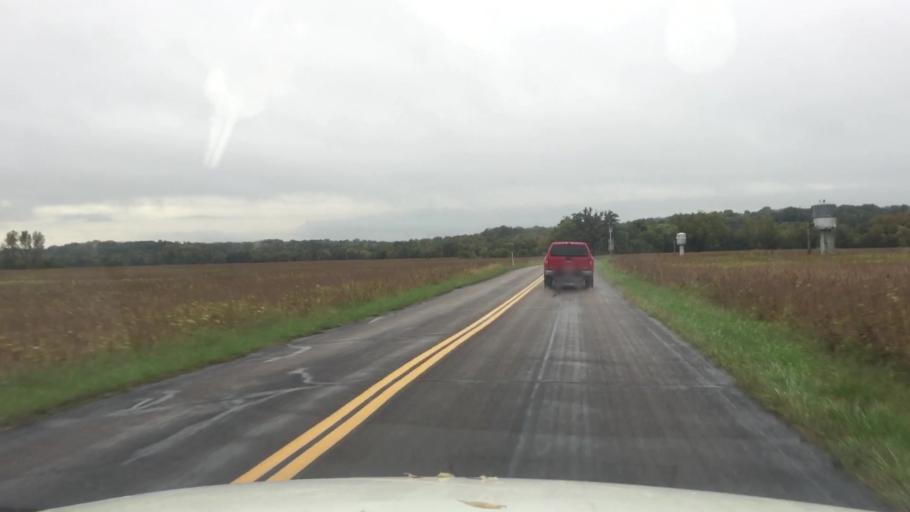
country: US
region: Missouri
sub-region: Boone County
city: Columbia
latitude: 38.8949
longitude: -92.4647
